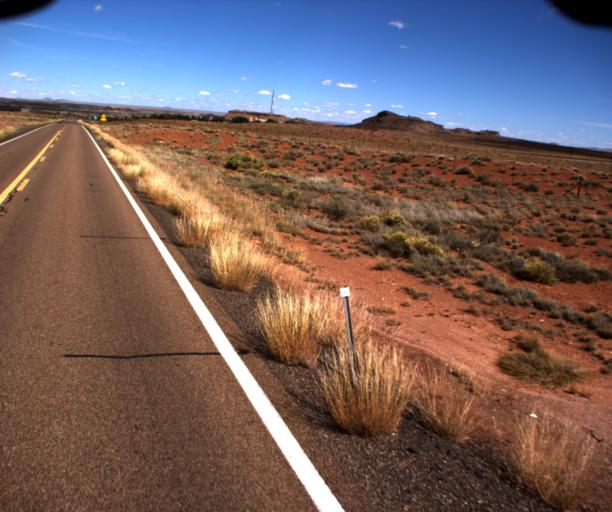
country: US
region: Arizona
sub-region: Navajo County
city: Holbrook
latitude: 34.8594
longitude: -110.1675
